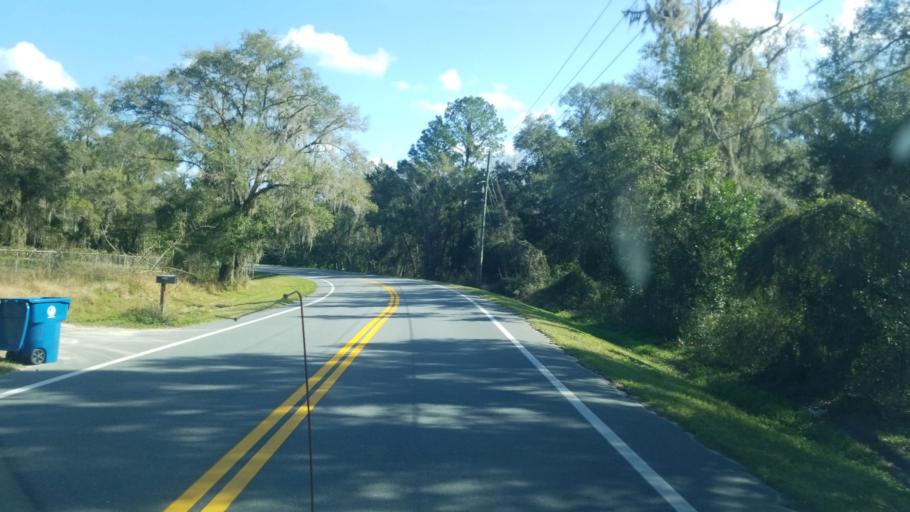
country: US
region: Florida
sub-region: Hernando County
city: North Brooksville
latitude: 28.6294
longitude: -82.3748
